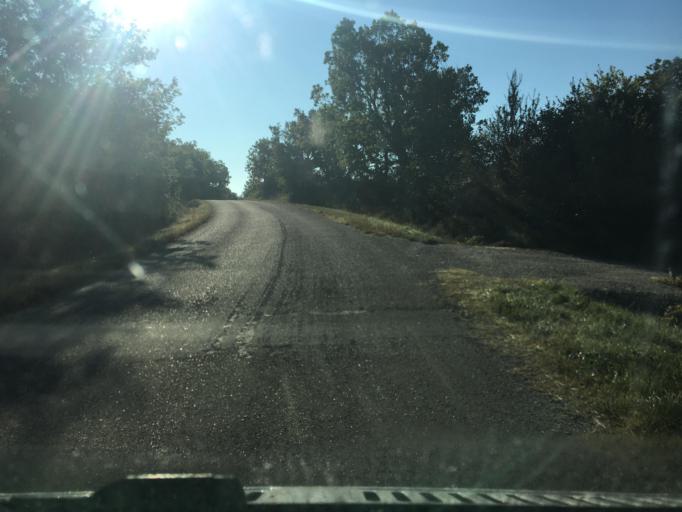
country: FR
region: Languedoc-Roussillon
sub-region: Departement du Gard
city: Barjac
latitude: 44.1771
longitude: 4.3394
